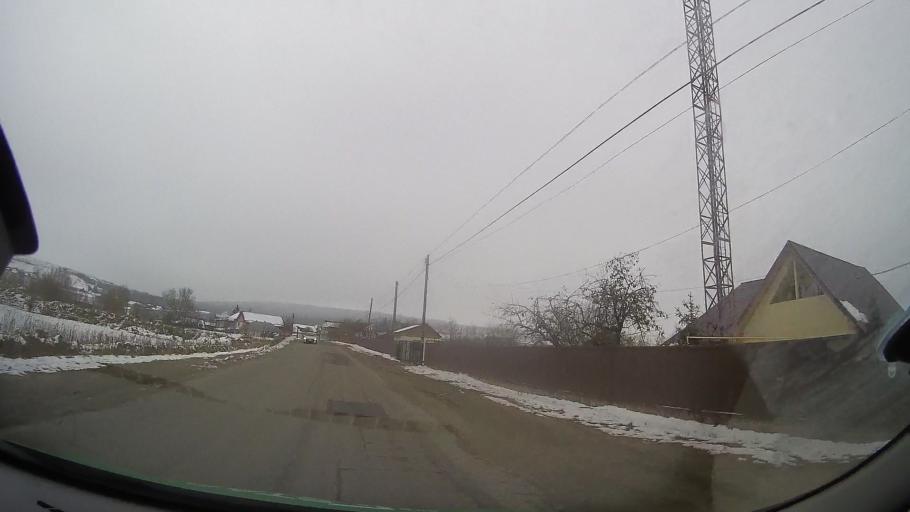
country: RO
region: Bacau
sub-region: Comuna Podu Turcului
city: Podu Turcului
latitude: 46.2061
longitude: 27.3809
